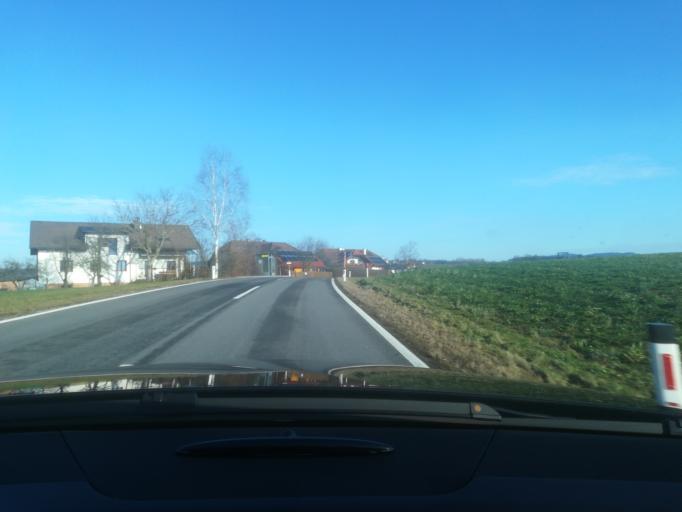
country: AT
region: Upper Austria
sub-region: Politischer Bezirk Urfahr-Umgebung
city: Herzogsdorf
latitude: 48.4182
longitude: 14.0940
